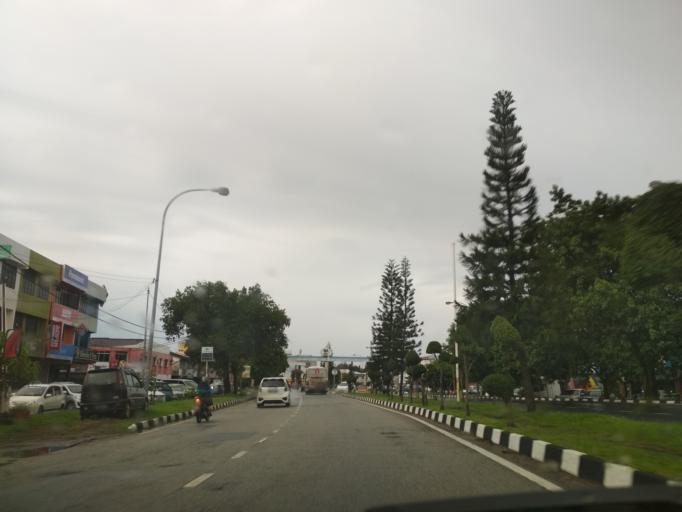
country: MY
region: Perlis
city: Kangar
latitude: 6.4342
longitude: 100.1877
